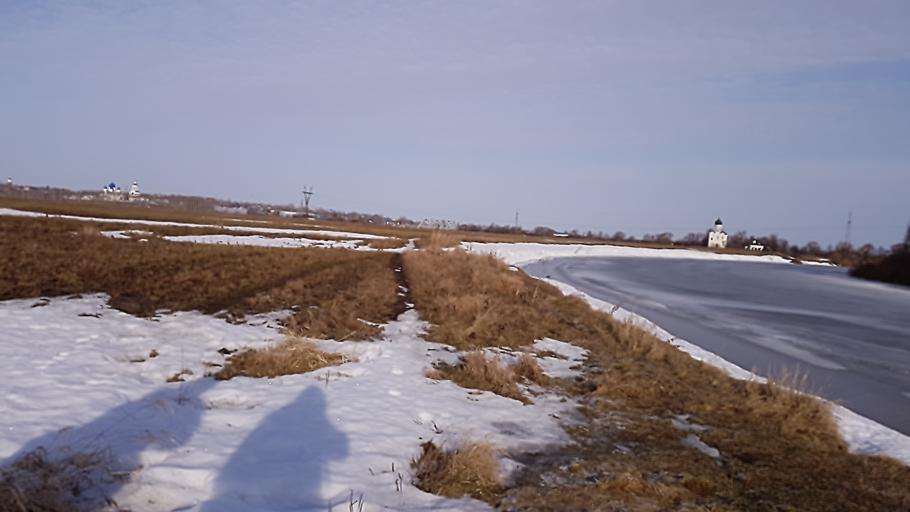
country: RU
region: Vladimir
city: Bogolyubovo
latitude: 56.1911
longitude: 40.5661
